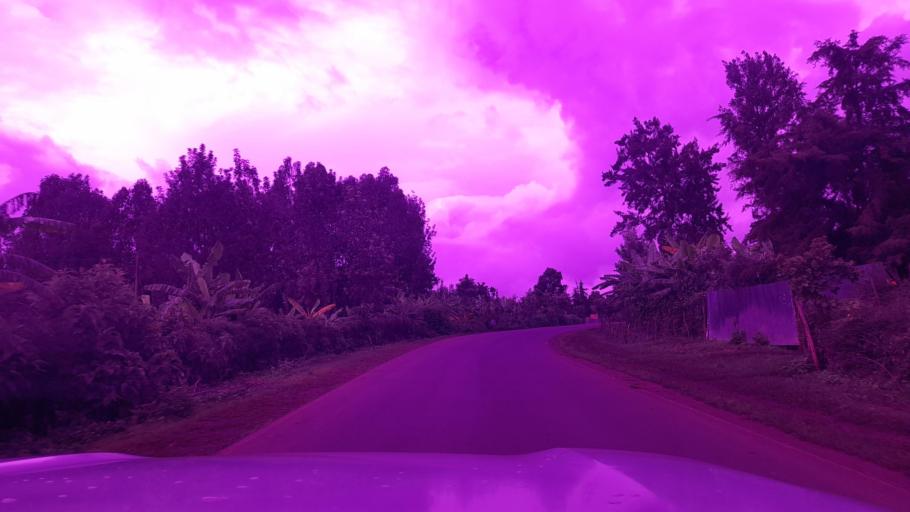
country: ET
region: Oromiya
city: Jima
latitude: 7.9044
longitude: 37.3905
